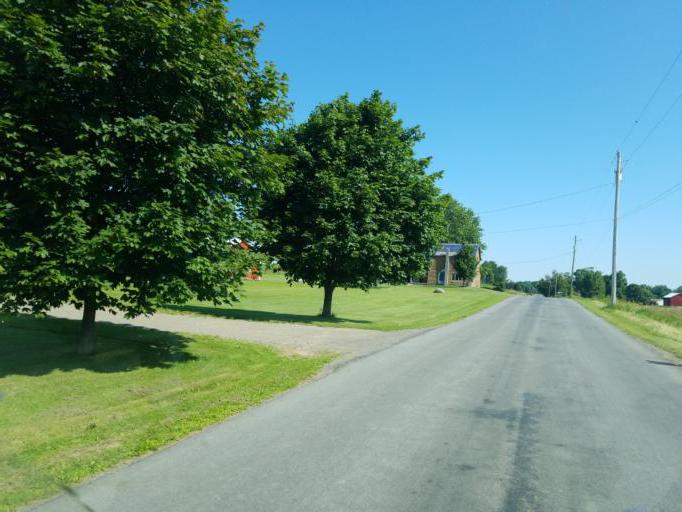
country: US
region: New York
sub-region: Wayne County
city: Clyde
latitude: 43.0655
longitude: -76.8755
